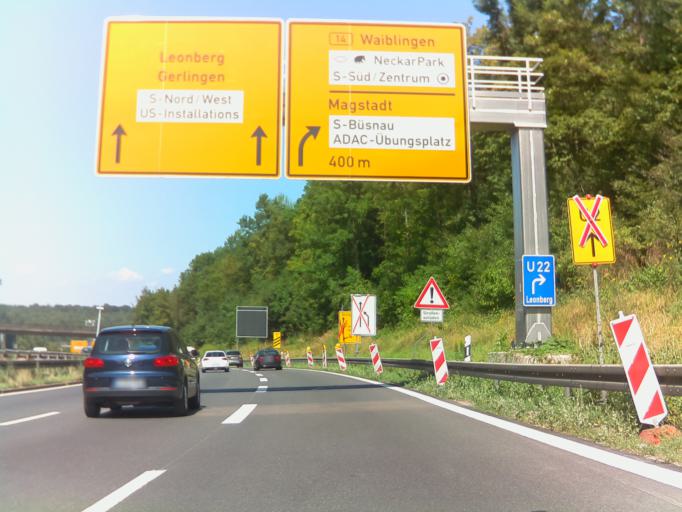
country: DE
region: Baden-Wuerttemberg
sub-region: Regierungsbezirk Stuttgart
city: Stuttgart
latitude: 48.7503
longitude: 9.1159
